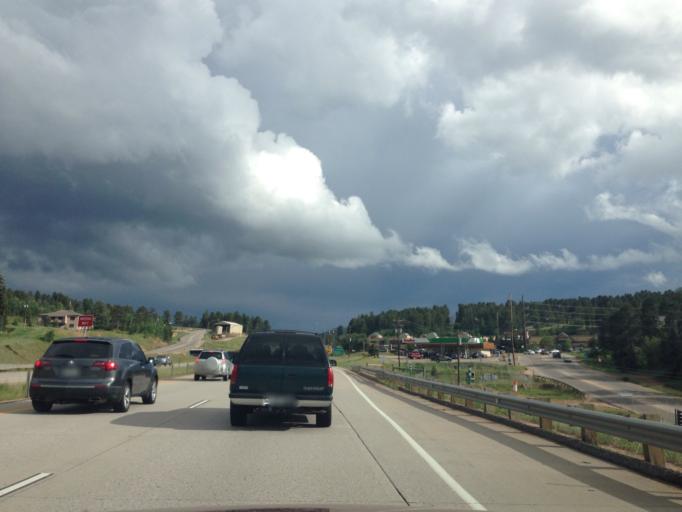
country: US
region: Colorado
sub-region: Jefferson County
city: Evergreen
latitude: 39.5224
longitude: -105.3063
